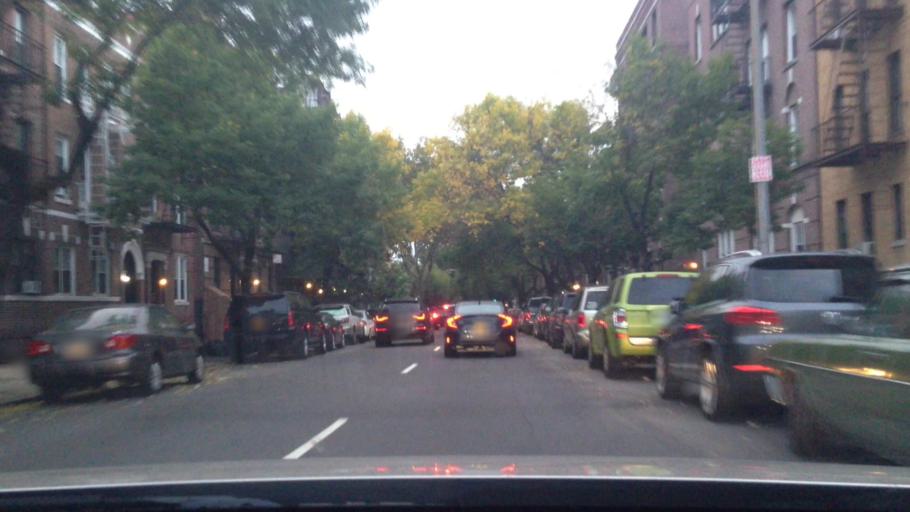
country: US
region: New York
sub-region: Queens County
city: Long Island City
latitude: 40.7616
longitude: -73.9236
